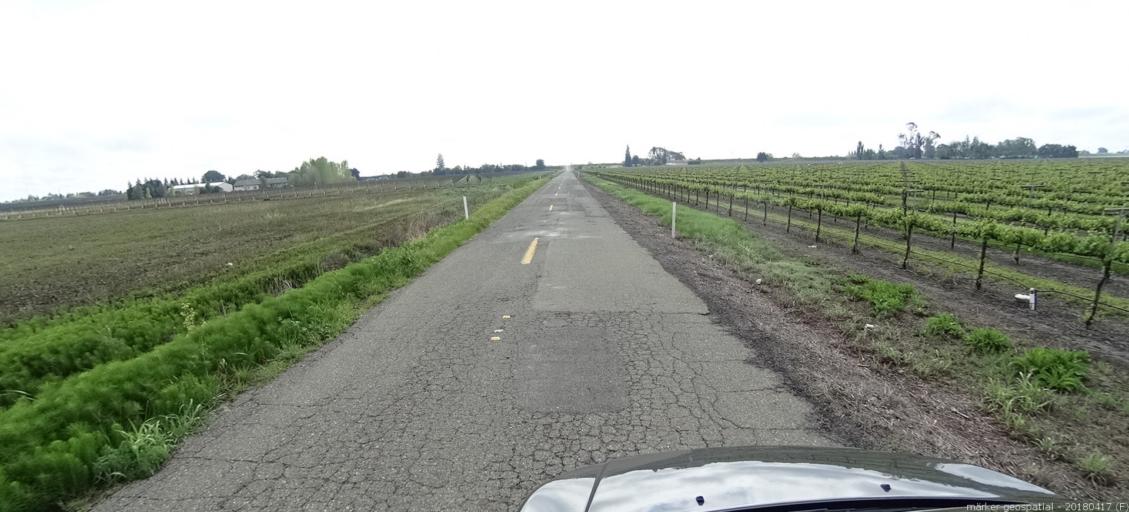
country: US
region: California
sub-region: Sacramento County
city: Walnut Grove
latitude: 38.2134
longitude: -121.5646
